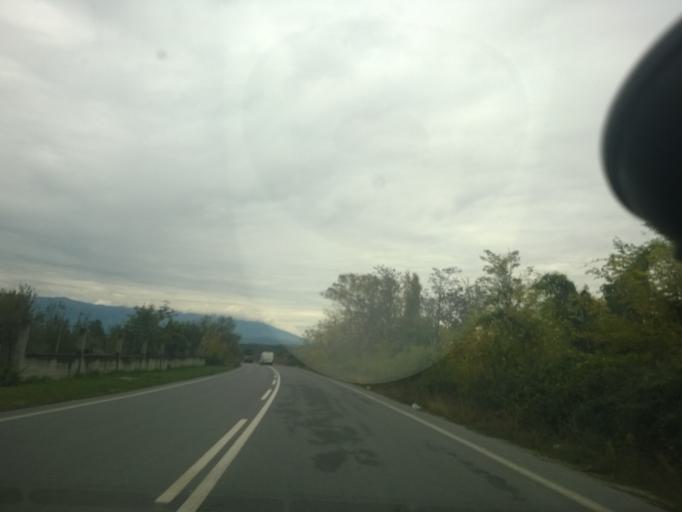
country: GR
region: Central Macedonia
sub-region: Nomos Pellis
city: Loutraki
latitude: 40.9711
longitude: 21.9784
